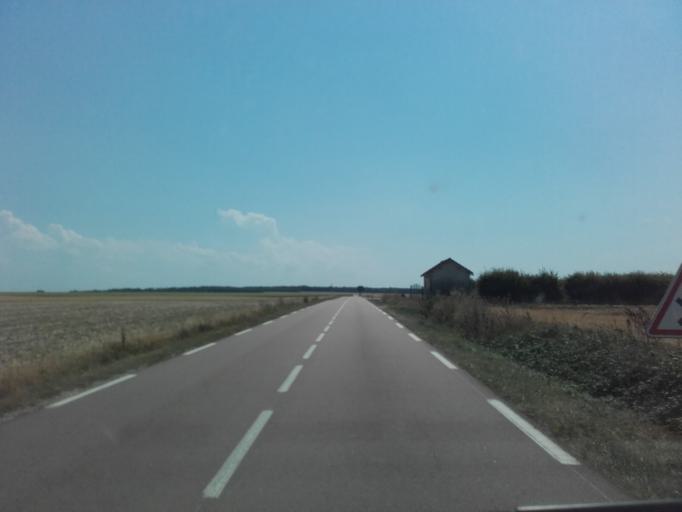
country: FR
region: Bourgogne
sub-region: Departement de l'Yonne
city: Joux-la-Ville
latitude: 47.7244
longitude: 3.8533
